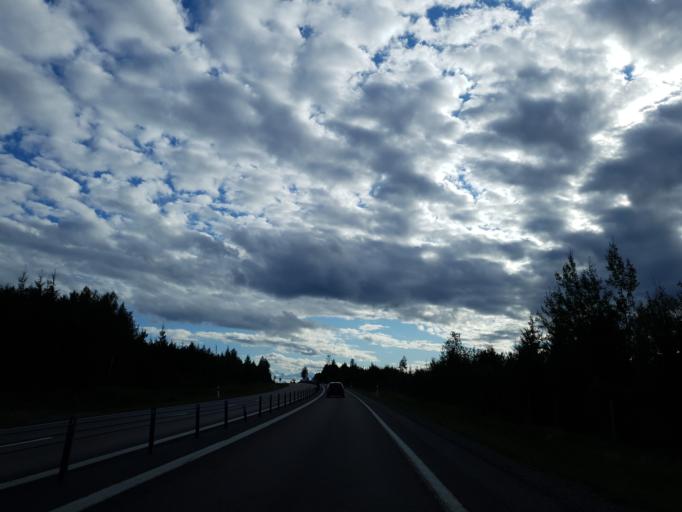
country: SE
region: Vaesternorrland
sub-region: Haernoesands Kommun
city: Haernoesand
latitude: 62.6056
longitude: 17.8200
